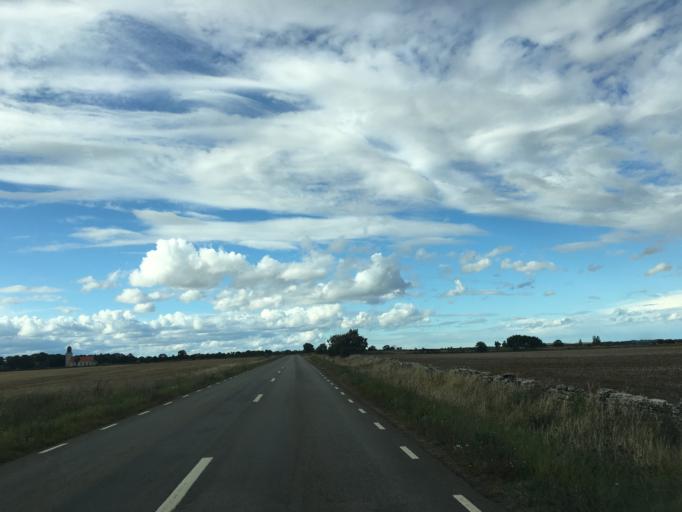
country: SE
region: Kalmar
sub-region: Morbylanga Kommun
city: Moerbylanga
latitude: 56.3998
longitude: 16.4364
